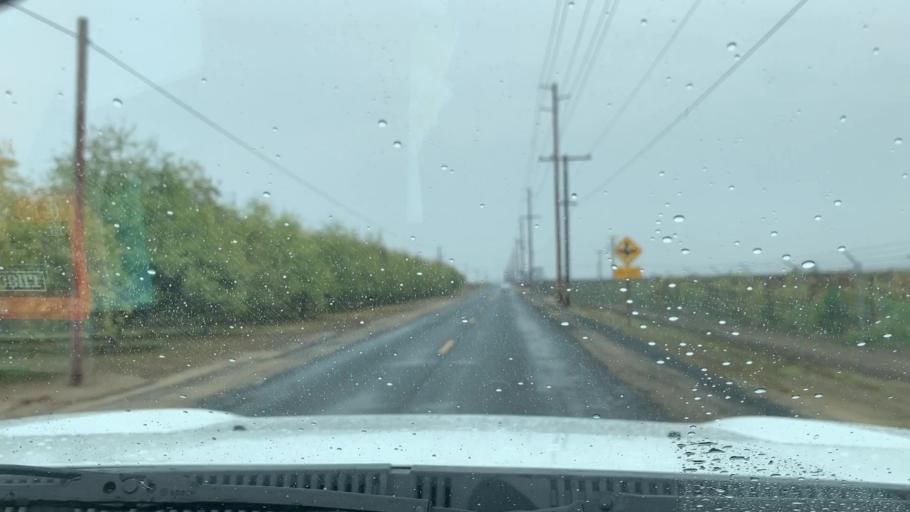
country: US
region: California
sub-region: Tulare County
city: Earlimart
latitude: 35.8339
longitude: -119.2346
